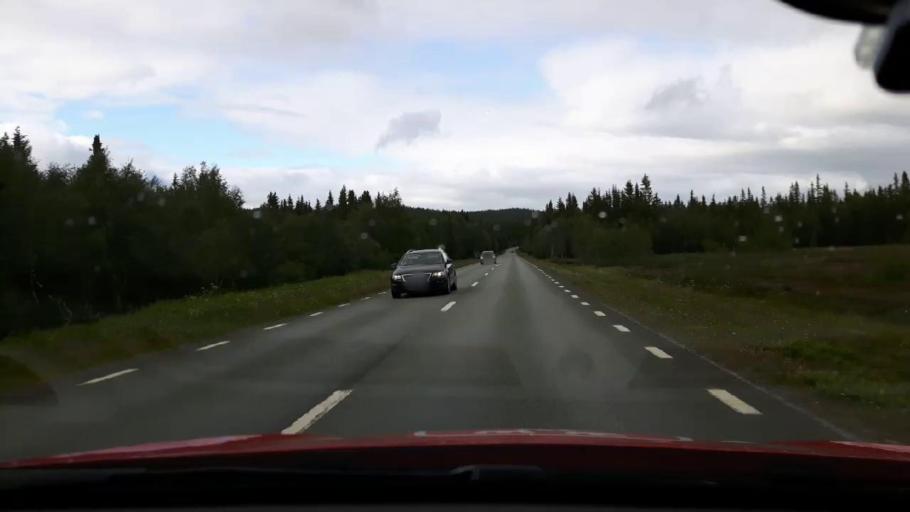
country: SE
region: Jaemtland
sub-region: Are Kommun
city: Are
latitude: 63.3672
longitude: 12.7021
